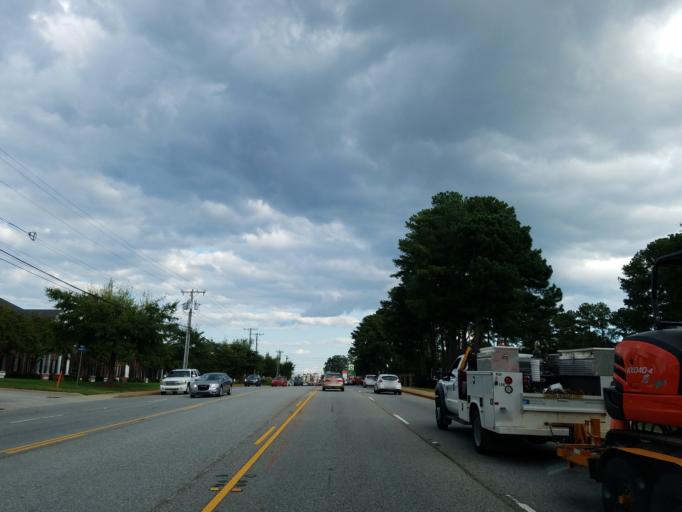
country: US
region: South Carolina
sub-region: Greenville County
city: Taylors
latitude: 34.8613
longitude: -82.2746
